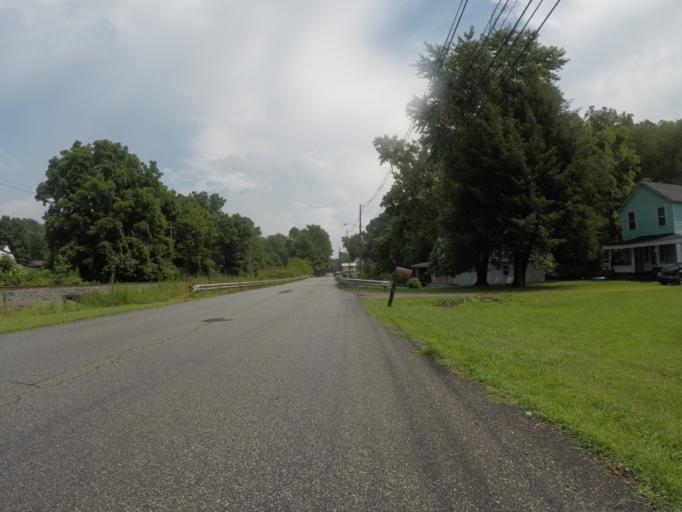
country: US
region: Kentucky
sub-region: Boyd County
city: Westwood
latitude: 38.4696
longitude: -82.6713
